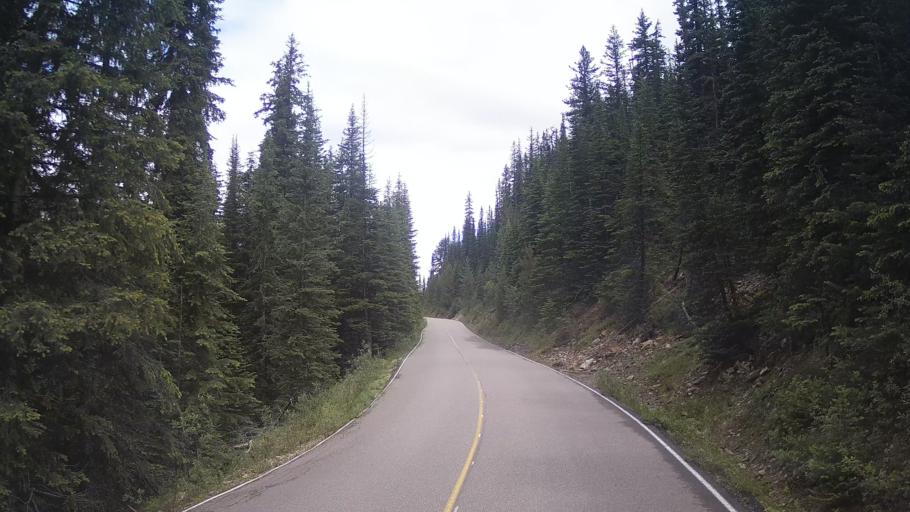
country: CA
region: Alberta
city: Jasper Park Lodge
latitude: 52.6925
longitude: -118.0577
